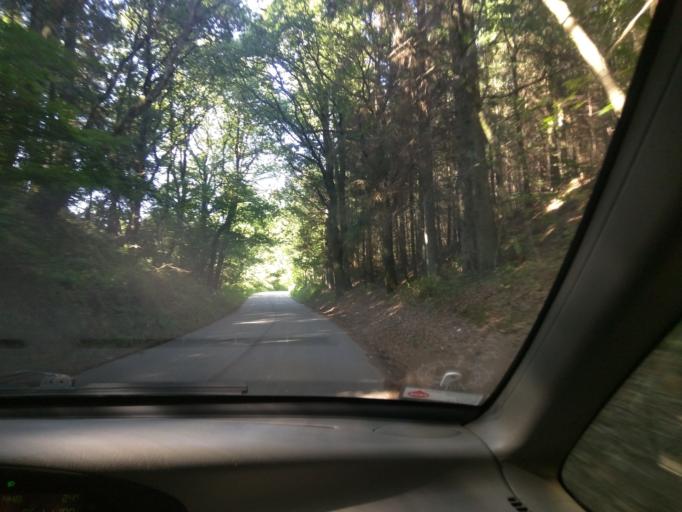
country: DK
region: Central Jutland
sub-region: Viborg Kommune
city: Bjerringbro
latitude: 56.4671
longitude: 9.6200
